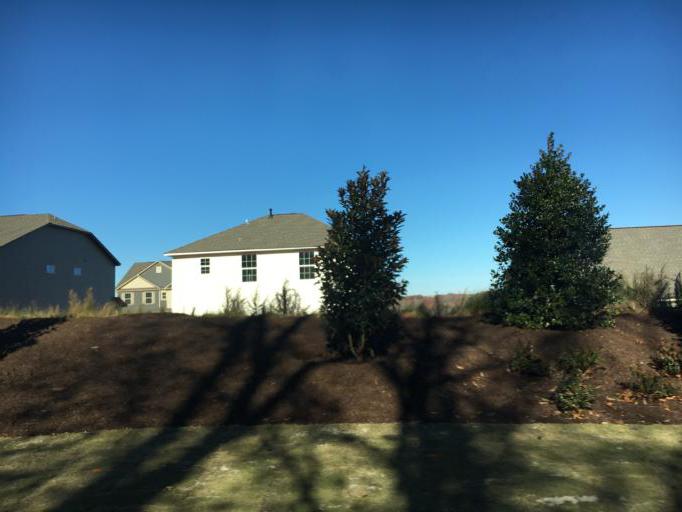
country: US
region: South Carolina
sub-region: Spartanburg County
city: Duncan
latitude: 34.8944
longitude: -82.1218
